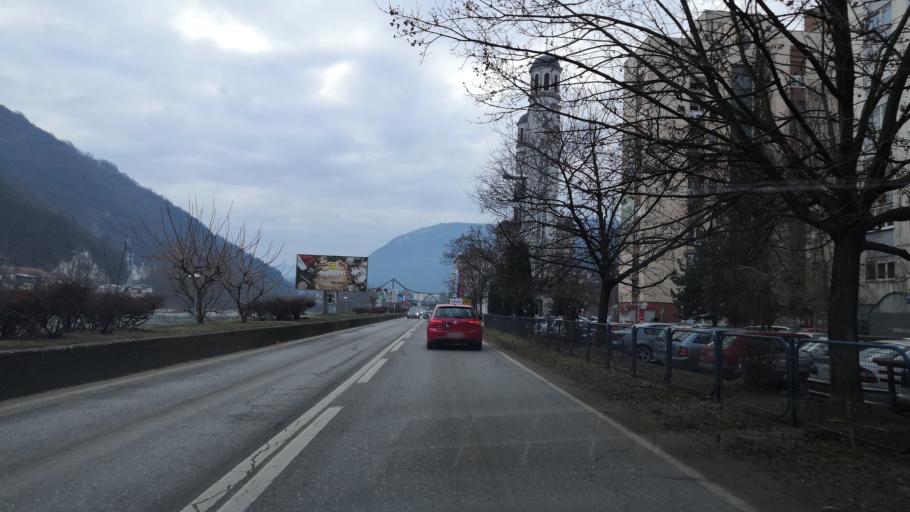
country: BA
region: Republika Srpska
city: Zvornik
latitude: 44.3896
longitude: 19.1055
